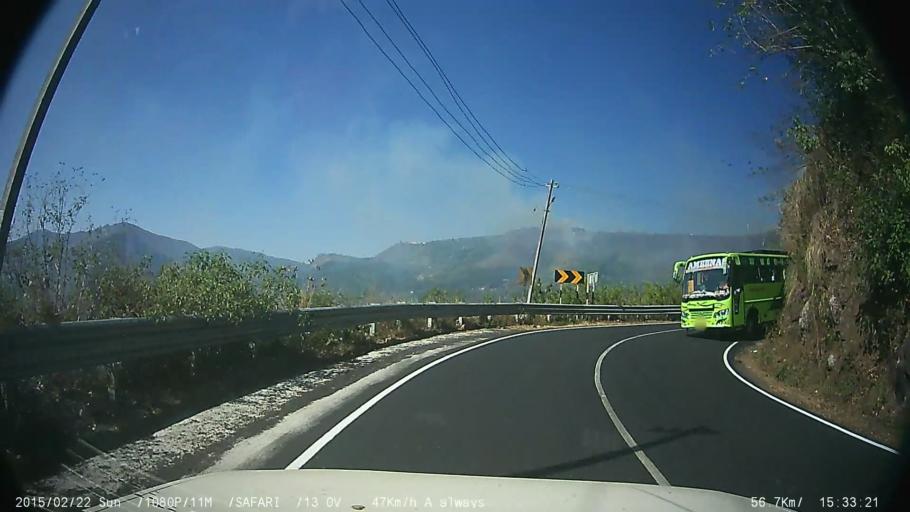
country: IN
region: Kerala
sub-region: Kottayam
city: Erattupetta
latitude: 9.5549
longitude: 76.9656
